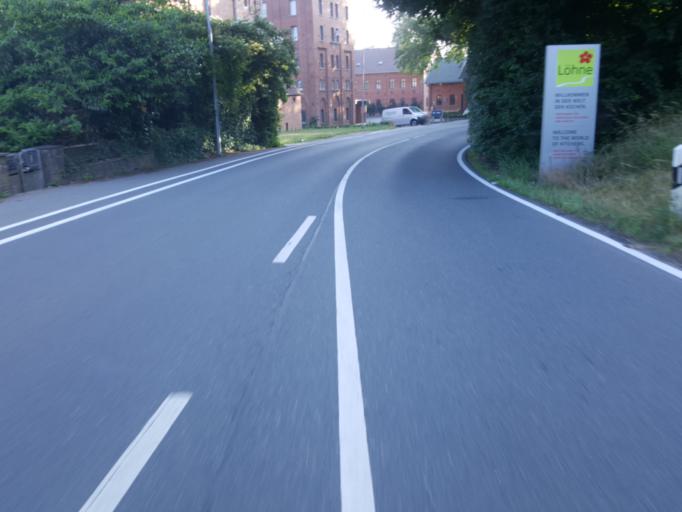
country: DE
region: North Rhine-Westphalia
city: Loehne
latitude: 52.1856
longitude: 8.6698
